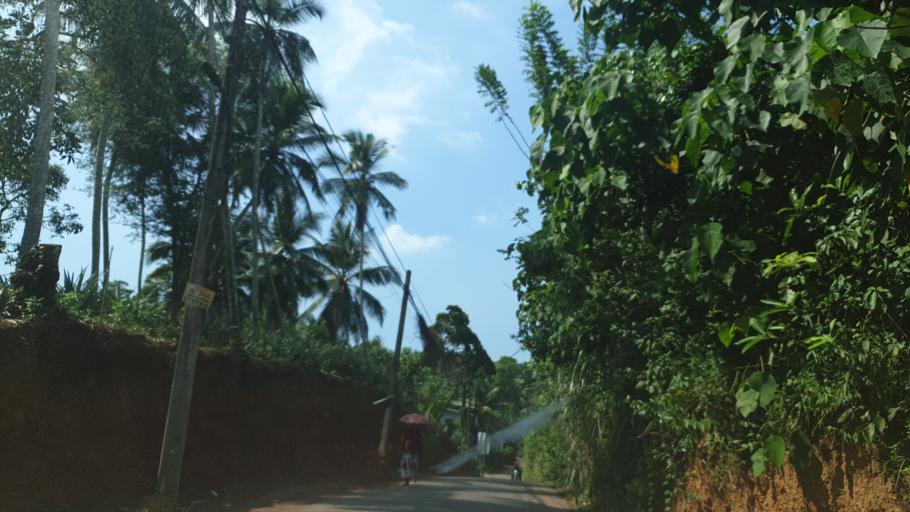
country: LK
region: Western
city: Panadura
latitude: 6.7228
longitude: 79.9557
